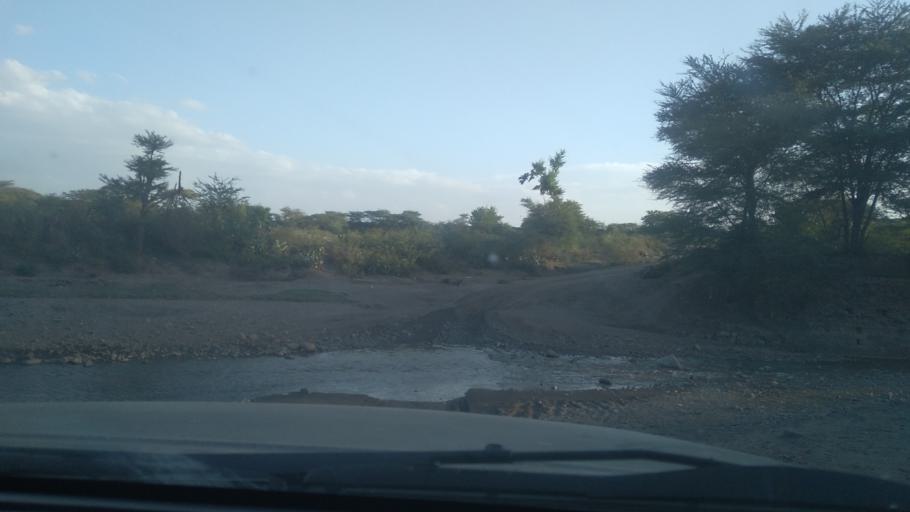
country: ET
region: Oromiya
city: Asbe Teferi
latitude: 9.2842
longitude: 40.8247
